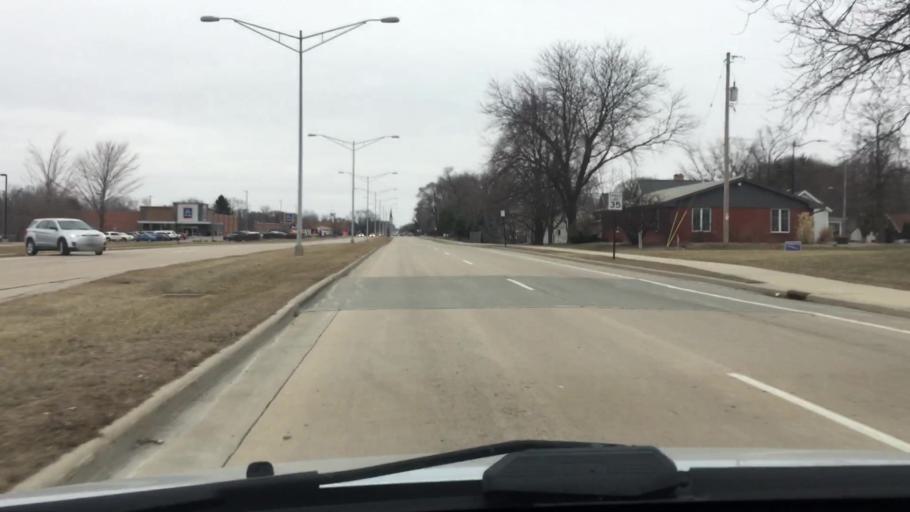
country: US
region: Wisconsin
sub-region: Jefferson County
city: Watertown
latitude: 43.1753
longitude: -88.7317
